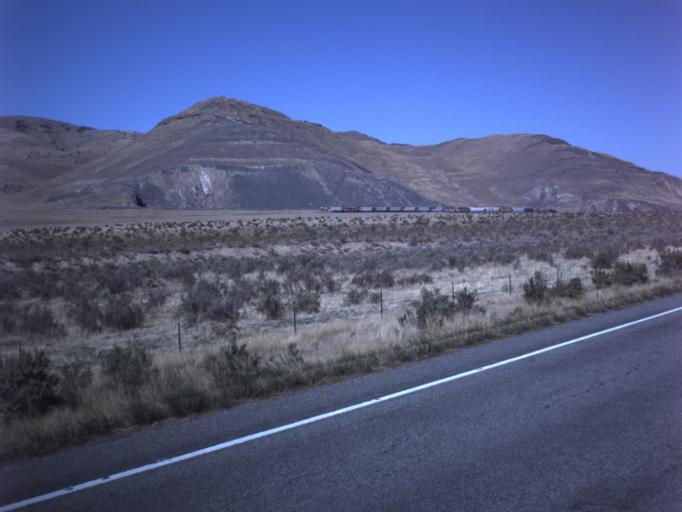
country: US
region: Utah
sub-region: Tooele County
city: Grantsville
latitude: 40.6671
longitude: -112.5441
